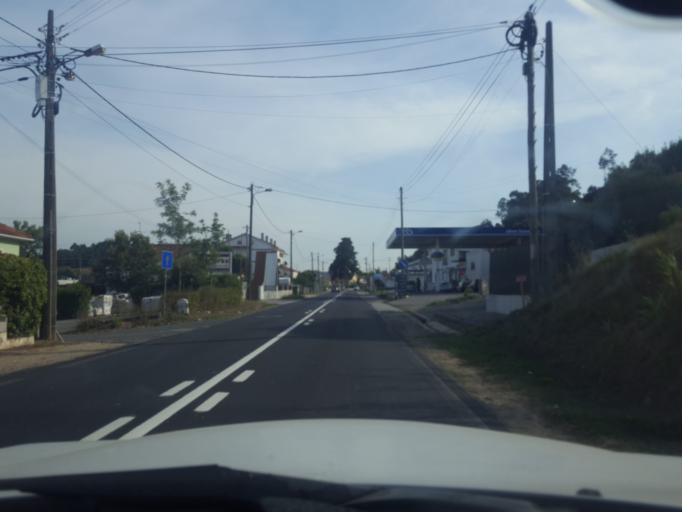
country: PT
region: Leiria
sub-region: Leiria
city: Leiria
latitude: 39.7153
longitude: -8.7889
